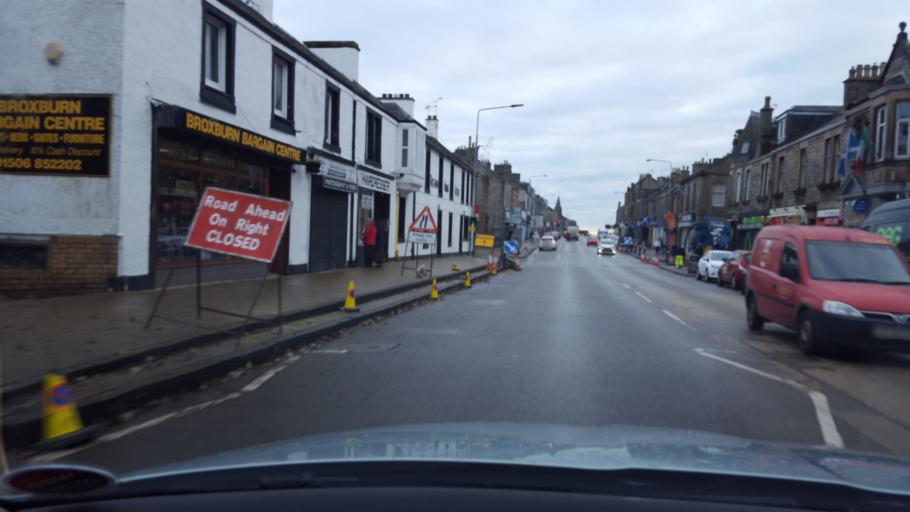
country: GB
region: Scotland
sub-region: West Lothian
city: Broxburn
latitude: 55.9342
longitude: -3.4723
